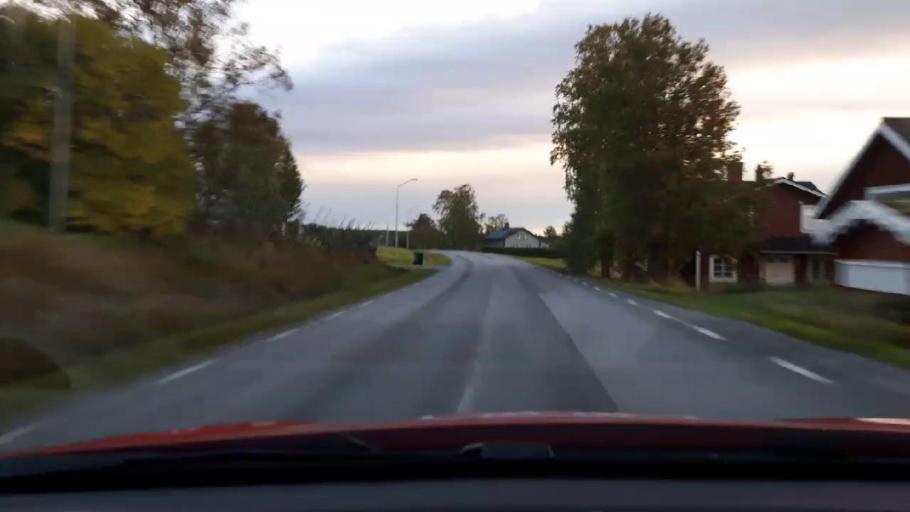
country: SE
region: Jaemtland
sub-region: OEstersunds Kommun
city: Ostersund
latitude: 63.0886
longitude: 14.4361
